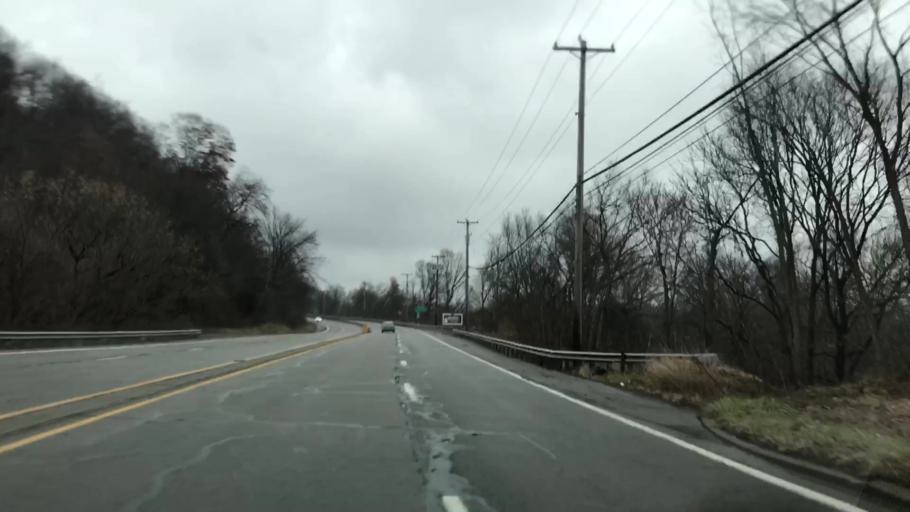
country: US
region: Pennsylvania
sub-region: Beaver County
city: Ambridge
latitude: 40.5815
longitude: -80.2375
